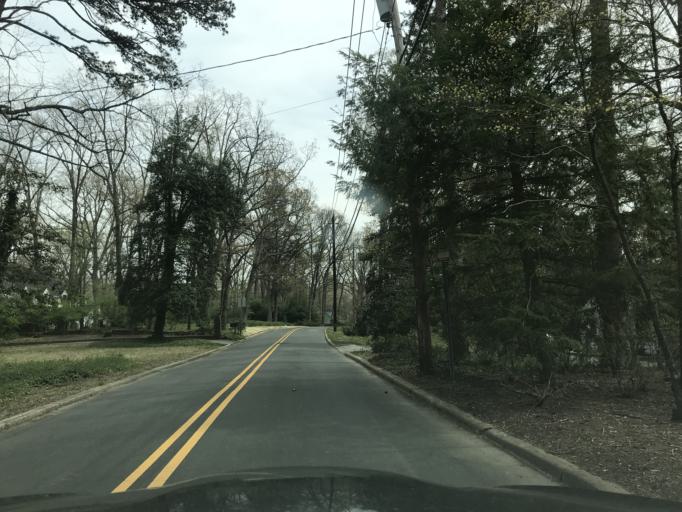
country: US
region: North Carolina
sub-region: Orange County
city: Chapel Hill
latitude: 35.9042
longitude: -79.0379
